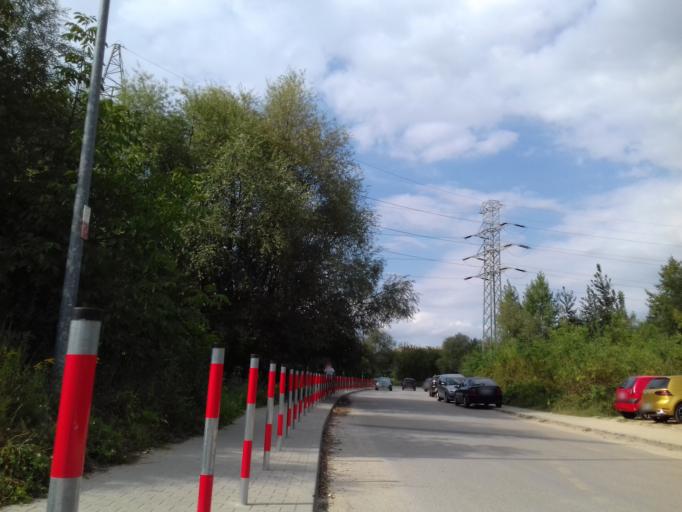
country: PL
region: Lesser Poland Voivodeship
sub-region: Krakow
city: Krakow
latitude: 50.0809
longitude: 19.9942
